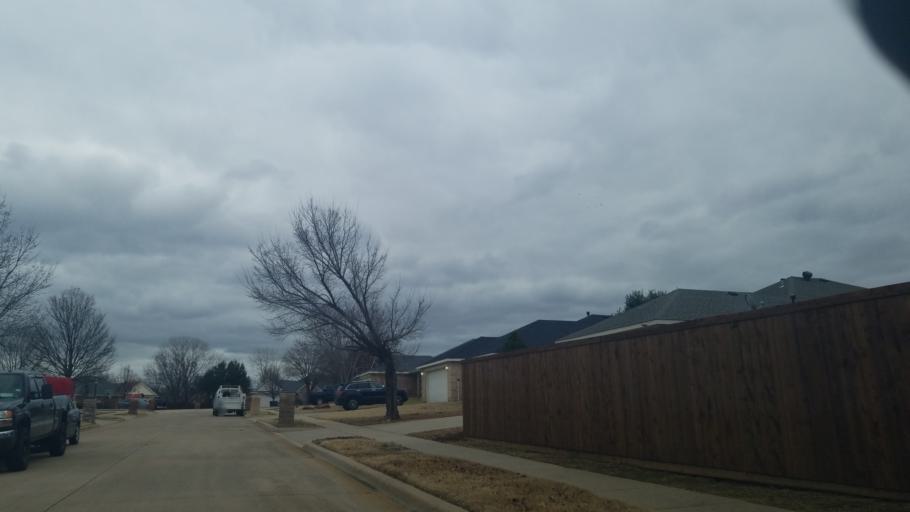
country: US
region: Texas
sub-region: Denton County
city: Corinth
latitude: 33.1345
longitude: -97.0887
